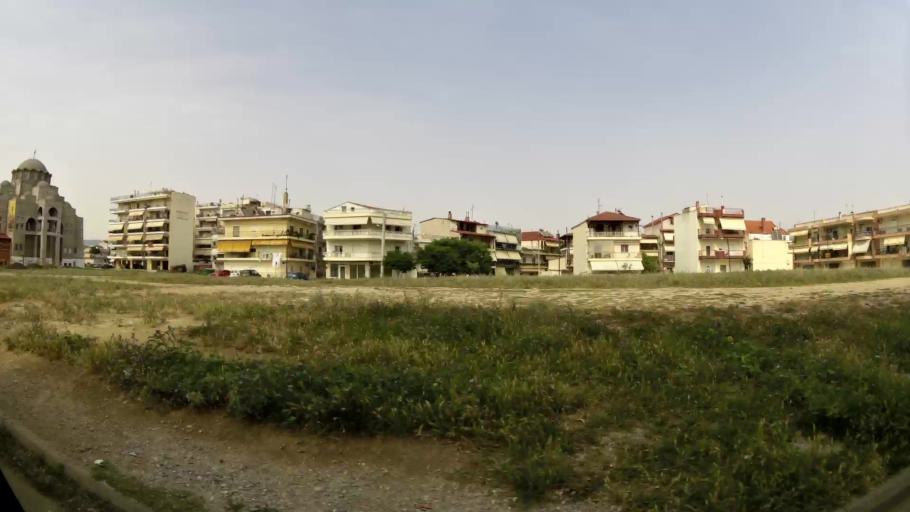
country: GR
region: Central Macedonia
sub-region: Nomos Thessalonikis
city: Stavroupoli
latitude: 40.6822
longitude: 22.9343
